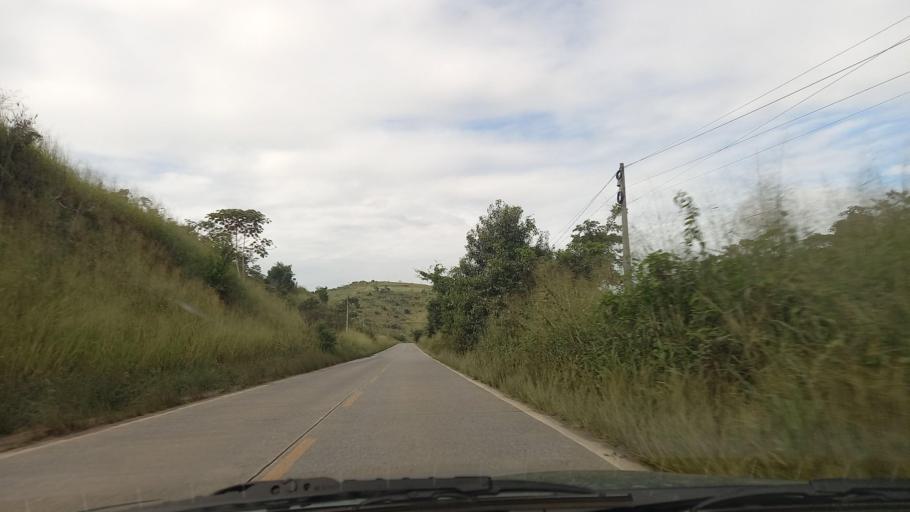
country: BR
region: Pernambuco
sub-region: Catende
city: Catende
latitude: -8.6916
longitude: -35.7111
